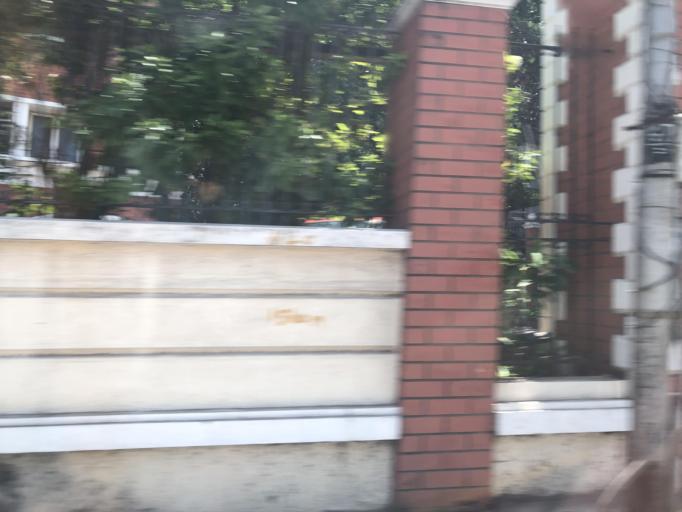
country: IN
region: Tamil Nadu
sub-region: Chennai
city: Gandhi Nagar
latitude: 13.0402
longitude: 80.2578
